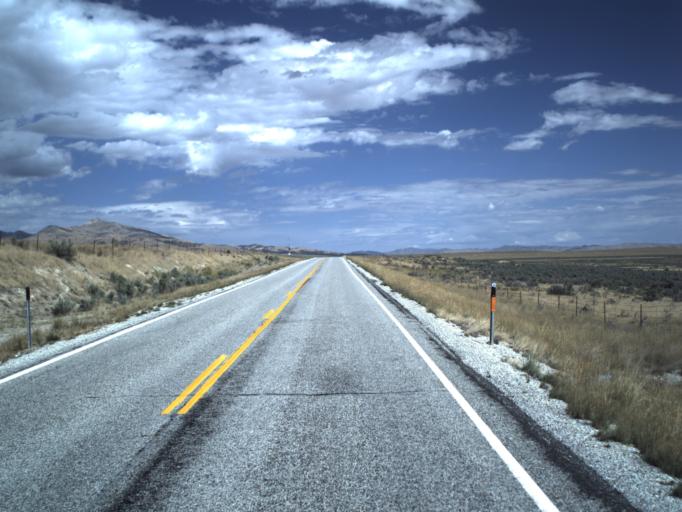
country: US
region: Idaho
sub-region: Oneida County
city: Malad City
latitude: 41.9351
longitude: -113.0872
